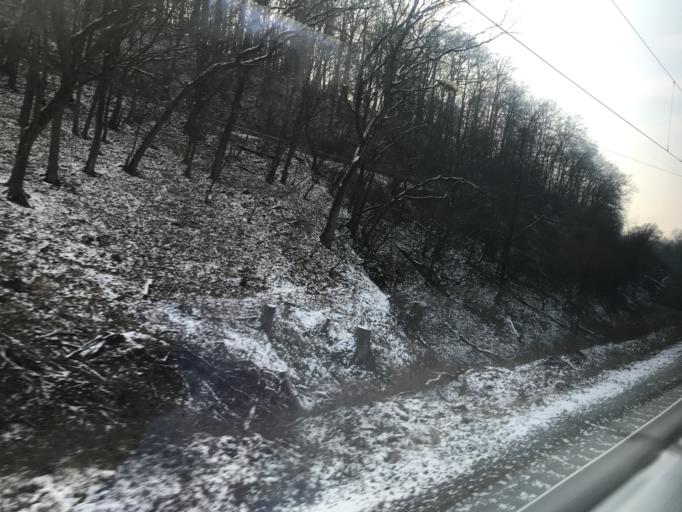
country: DE
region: Rheinland-Pfalz
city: Punderich
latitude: 50.0318
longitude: 7.1008
